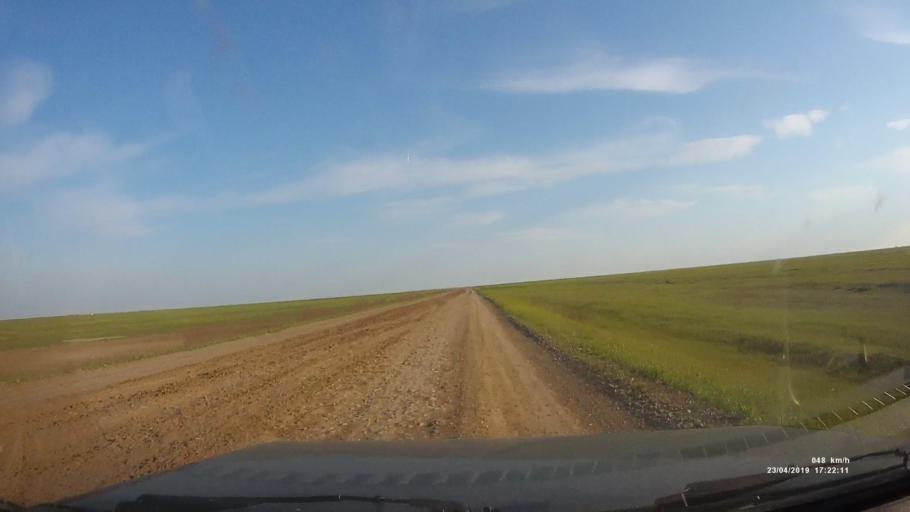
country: RU
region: Kalmykiya
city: Priyutnoye
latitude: 46.1706
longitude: 43.5062
